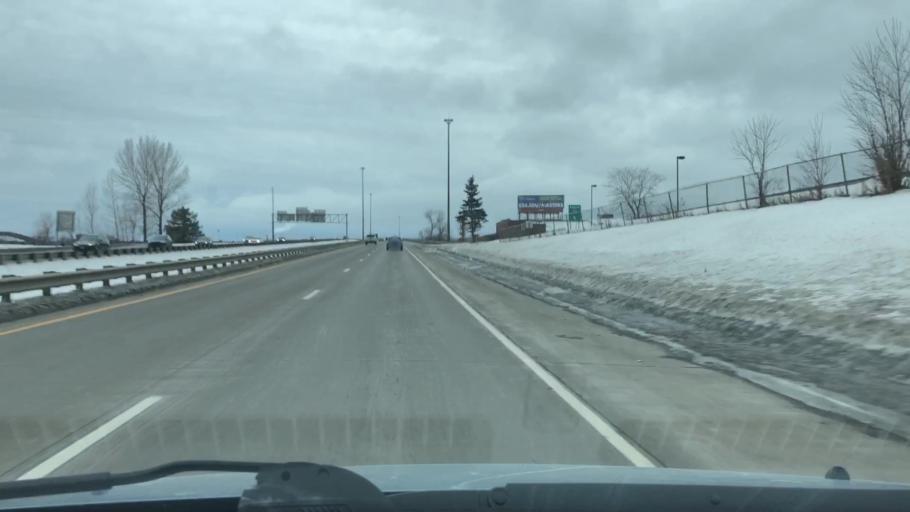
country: US
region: Minnesota
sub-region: Saint Louis County
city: Duluth
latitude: 46.7591
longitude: -92.1295
